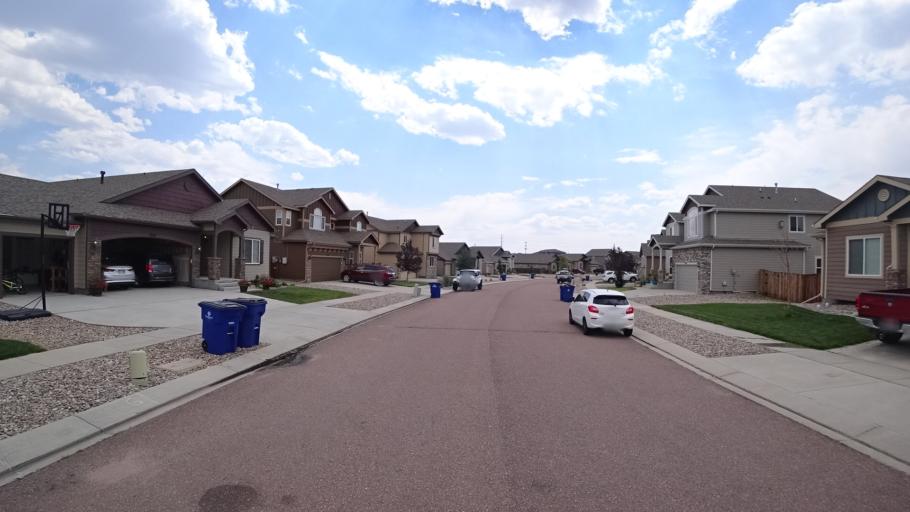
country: US
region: Colorado
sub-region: El Paso County
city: Black Forest
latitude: 38.9452
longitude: -104.6983
